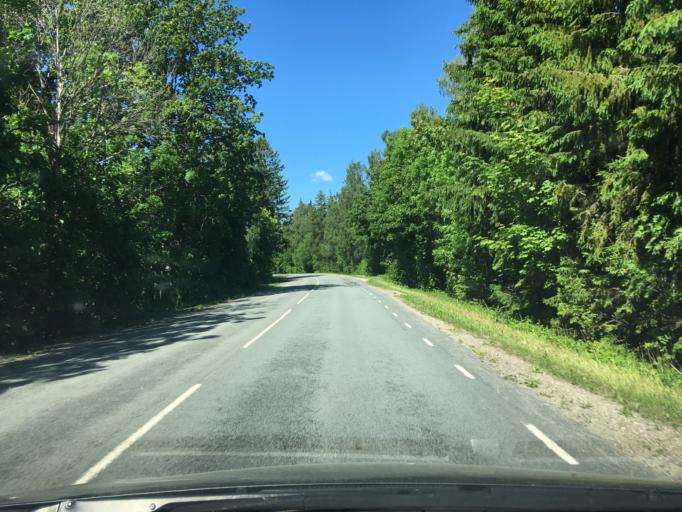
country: EE
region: Harju
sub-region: Rae vald
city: Vaida
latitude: 59.1976
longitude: 24.9689
